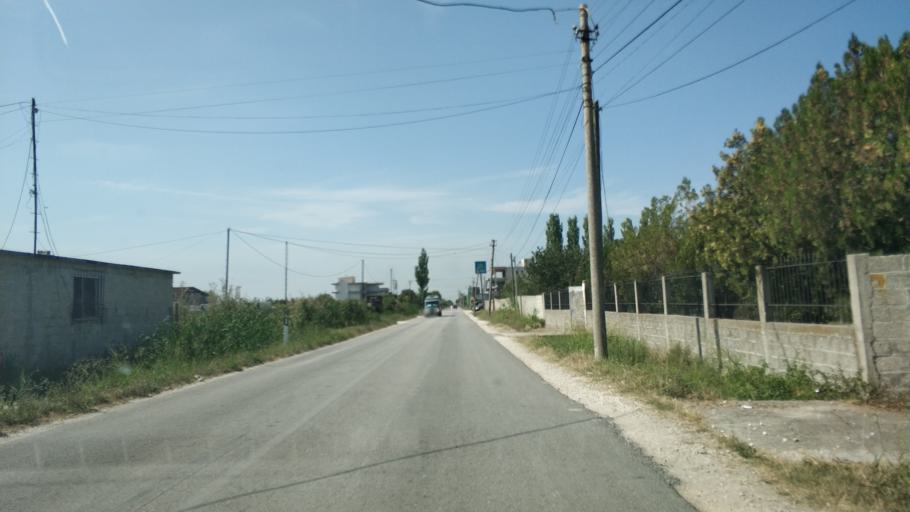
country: AL
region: Fier
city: Fier
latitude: 40.7312
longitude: 19.5387
